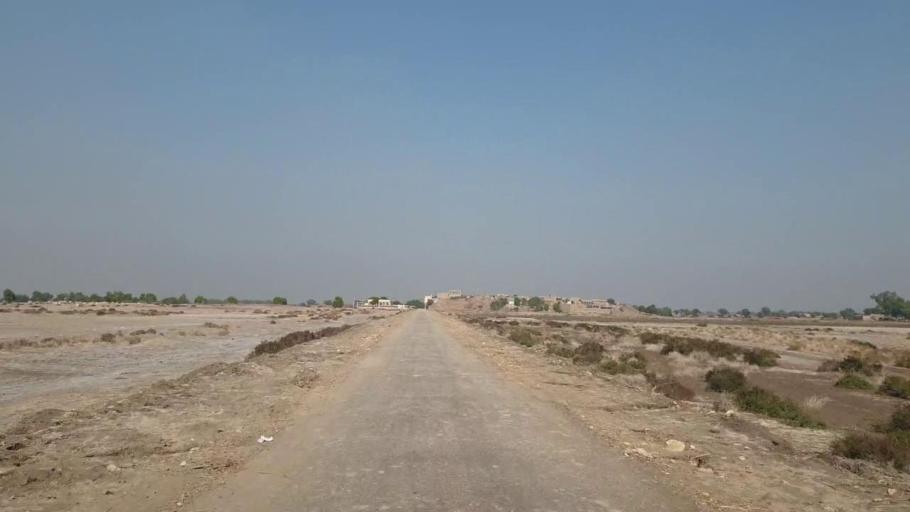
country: PK
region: Sindh
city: Sehwan
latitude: 26.4239
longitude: 67.7959
